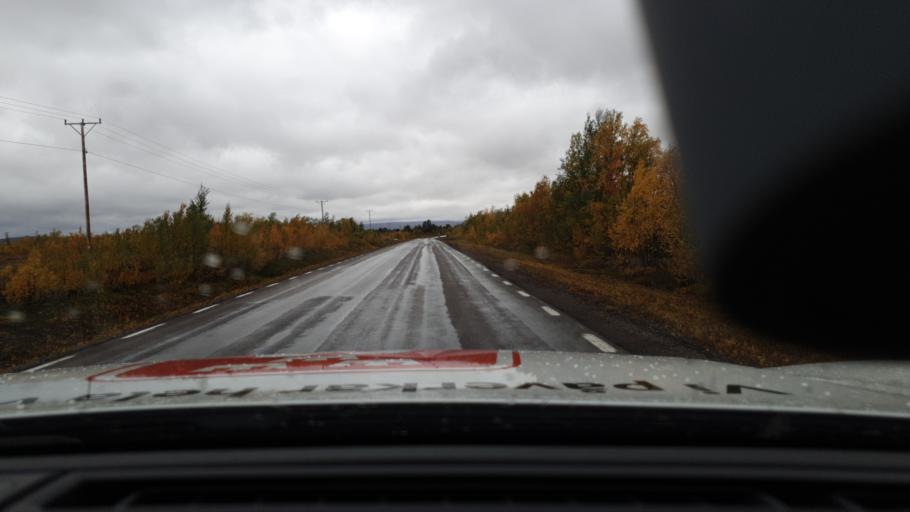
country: SE
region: Norrbotten
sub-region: Kiruna Kommun
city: Kiruna
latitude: 67.7657
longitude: 20.1456
